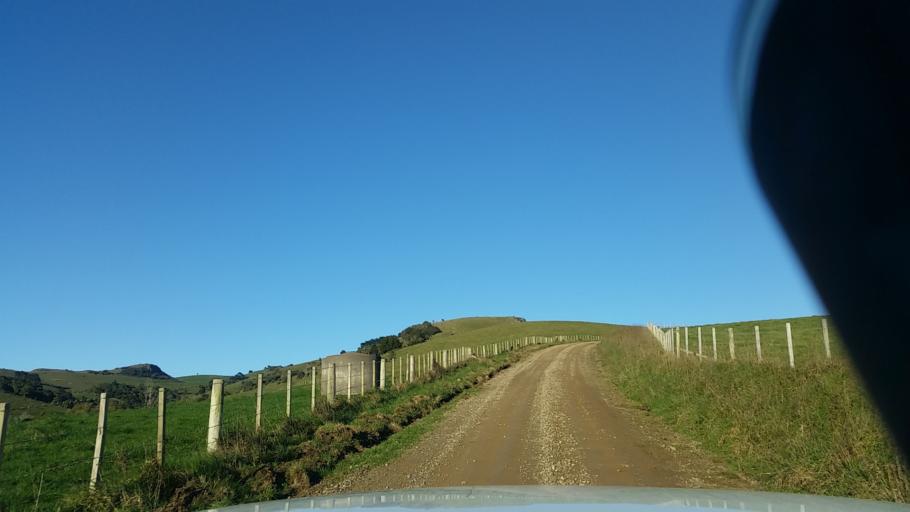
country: NZ
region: Canterbury
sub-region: Christchurch City
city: Christchurch
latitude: -43.6994
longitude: 173.0680
